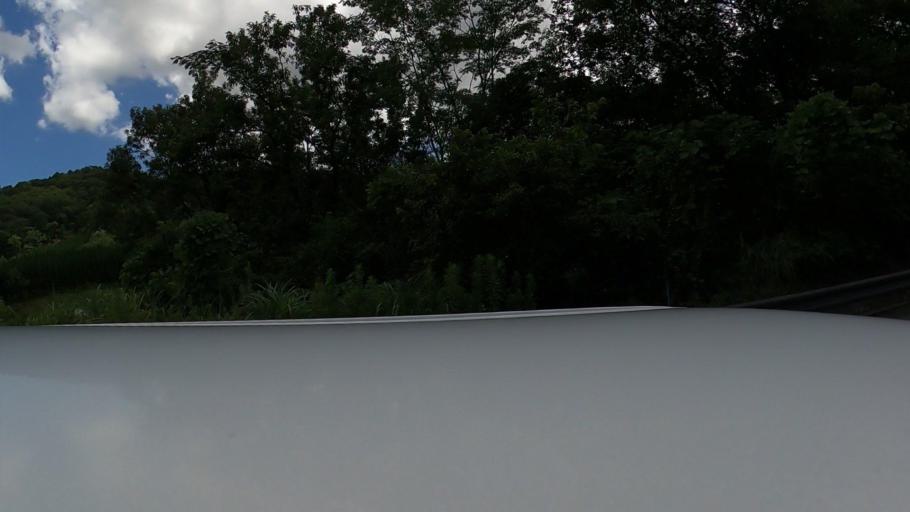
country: JP
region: Miyazaki
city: Nobeoka
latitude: 32.5796
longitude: 131.5203
